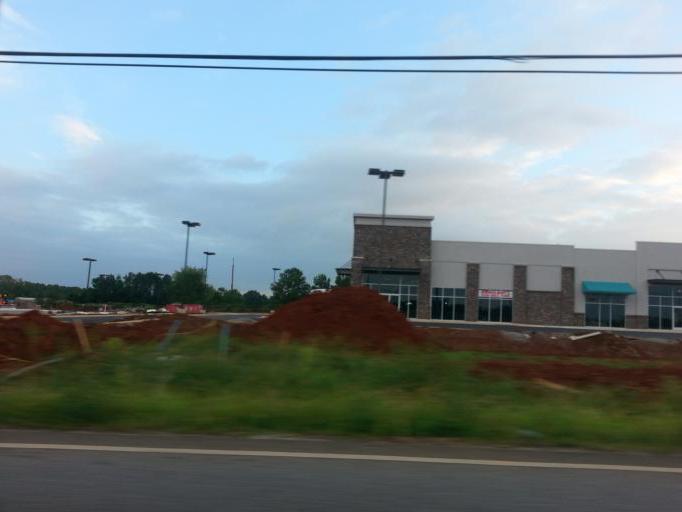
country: US
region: Alabama
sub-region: Madison County
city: Madison
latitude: 34.7543
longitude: -86.7113
